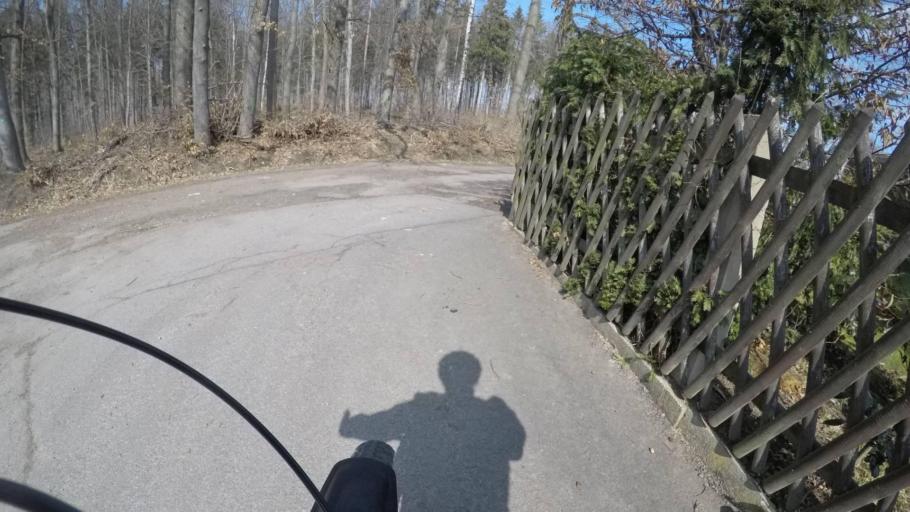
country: DE
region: Saxony
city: Limbach-Oberfrohna
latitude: 50.8689
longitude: 12.7700
